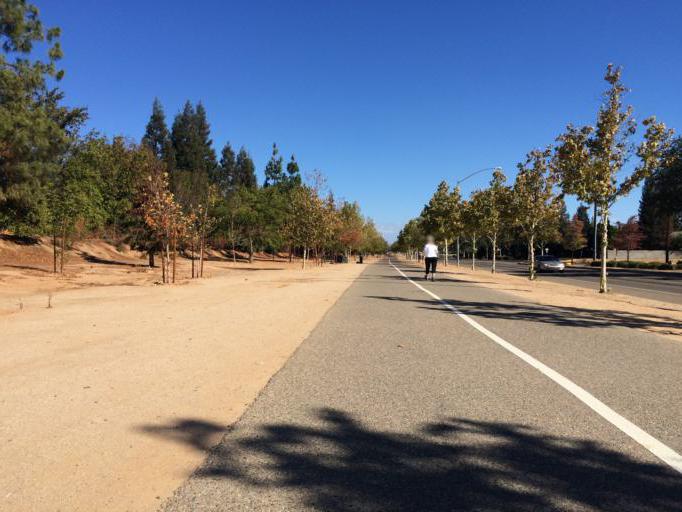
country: US
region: California
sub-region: Fresno County
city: Clovis
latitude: 36.8667
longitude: -119.7628
